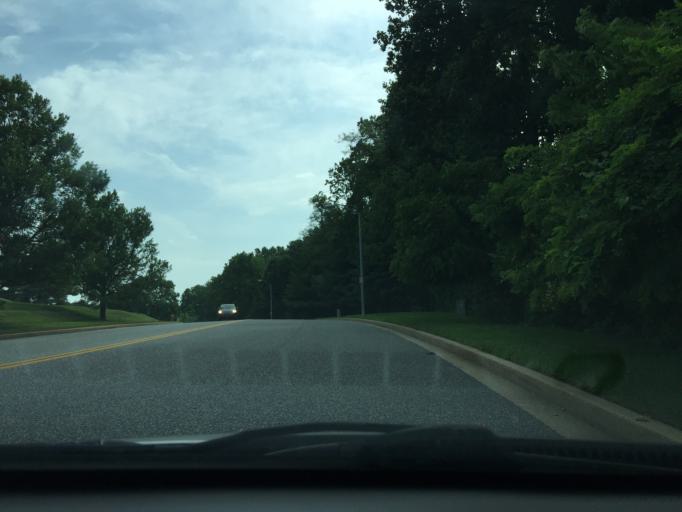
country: US
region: Maryland
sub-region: Baltimore County
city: Hunt Valley
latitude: 39.5200
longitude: -76.6487
